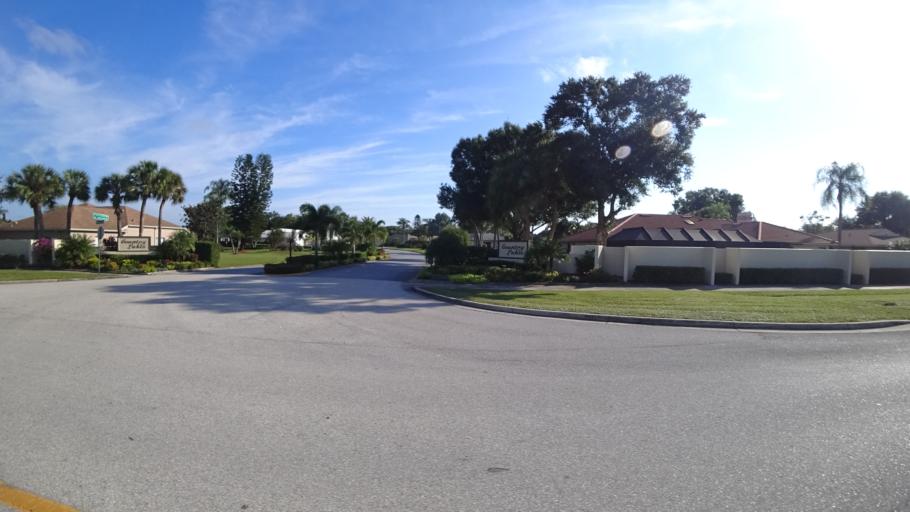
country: US
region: Florida
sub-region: Sarasota County
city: Desoto Lakes
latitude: 27.4169
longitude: -82.4920
